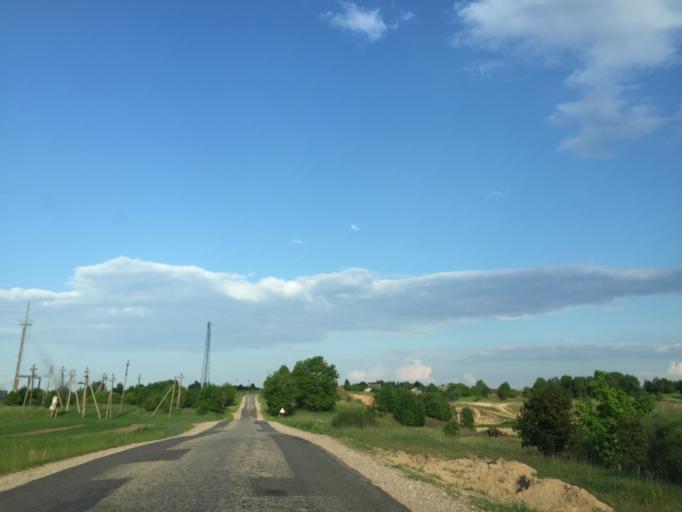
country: LT
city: Plateliai
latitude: 56.0465
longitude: 21.7977
